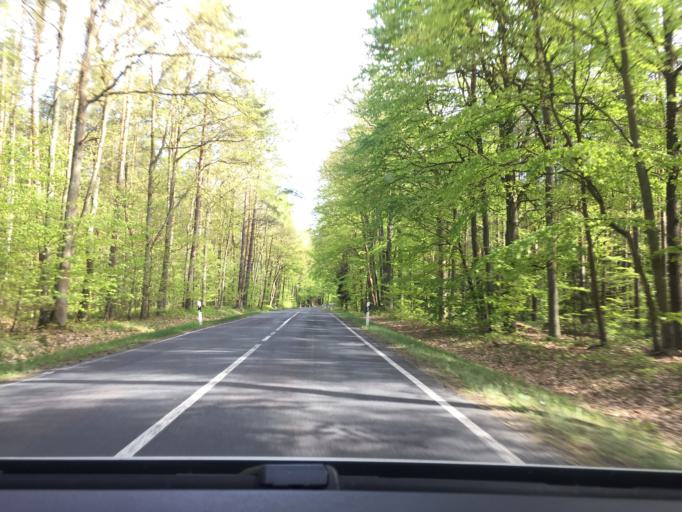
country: DE
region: Mecklenburg-Vorpommern
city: Torgelow
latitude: 53.6565
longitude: 14.0211
